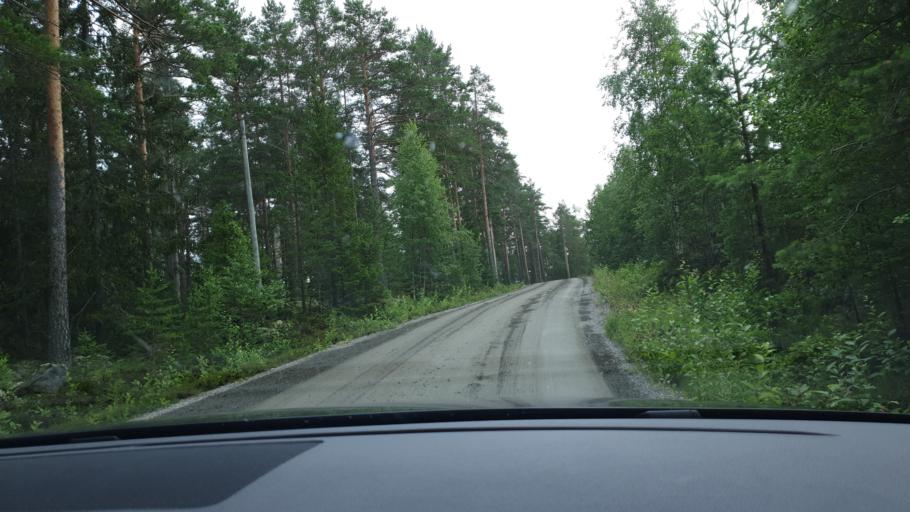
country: SE
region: Gaevleborg
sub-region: Hudiksvalls Kommun
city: Iggesund
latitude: 61.5201
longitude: 17.0176
